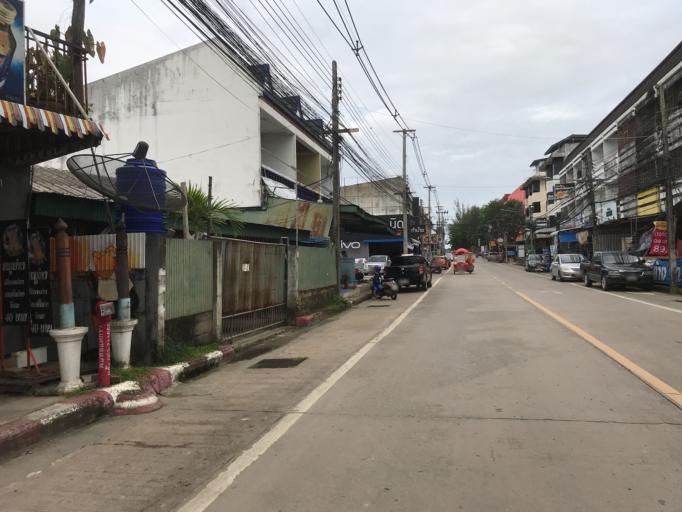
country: TH
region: Chiang Rai
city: Chiang Rai
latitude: 19.9029
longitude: 99.8153
